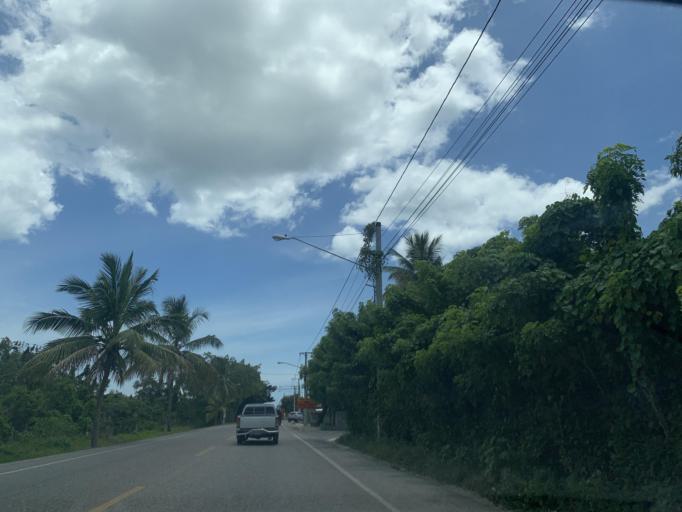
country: DO
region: Puerto Plata
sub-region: Puerto Plata
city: Puerto Plata
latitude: 19.7305
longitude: -70.6062
